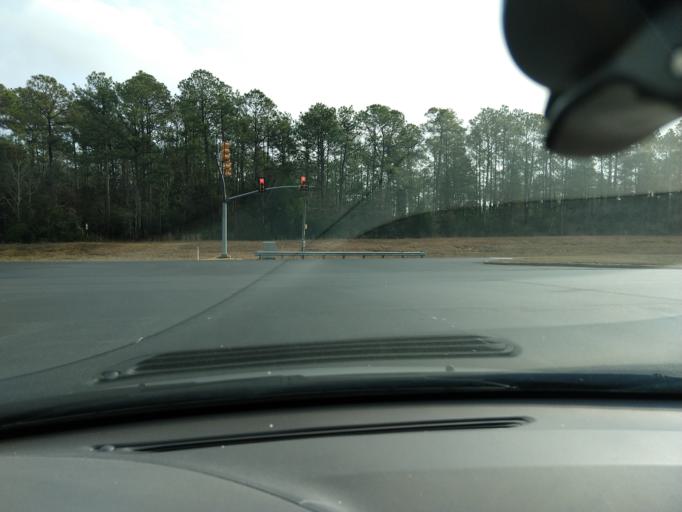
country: US
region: Mississippi
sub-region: Jackson County
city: Gulf Park Estates
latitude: 30.4388
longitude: -88.7174
